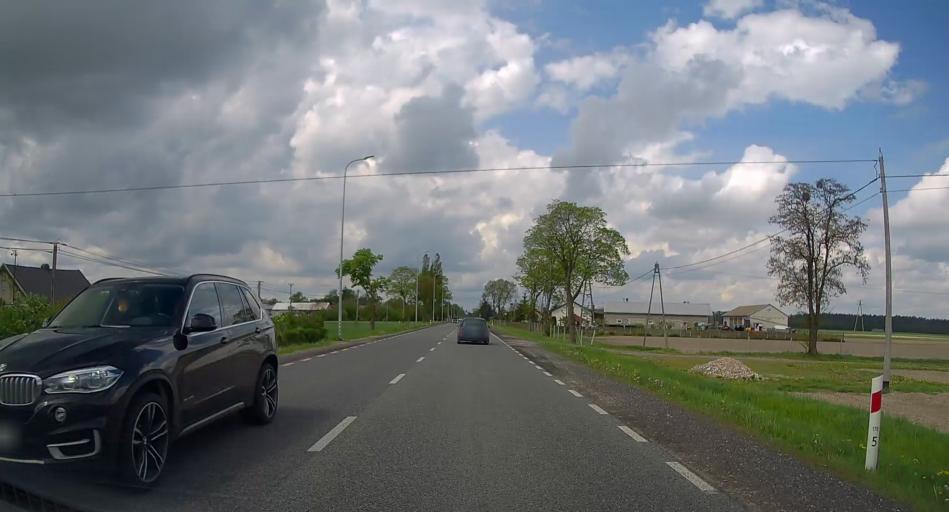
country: PL
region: Masovian Voivodeship
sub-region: Powiat plonski
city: Zaluski
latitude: 52.4449
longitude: 20.5192
